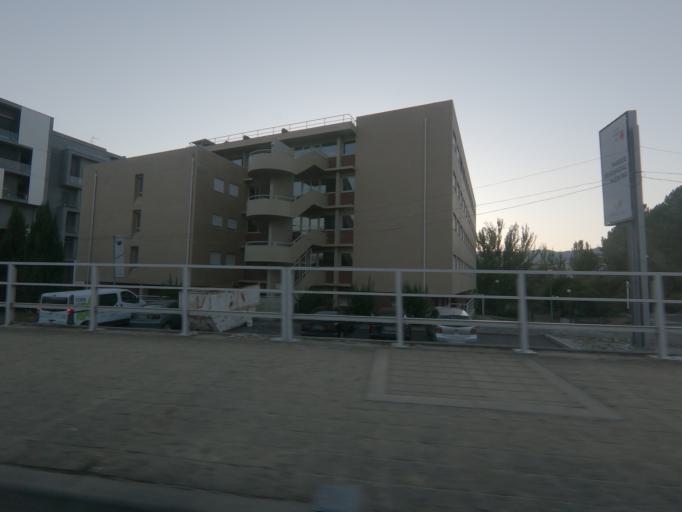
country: PT
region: Vila Real
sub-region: Vila Real
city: Vila Real
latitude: 41.3005
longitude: -7.7317
